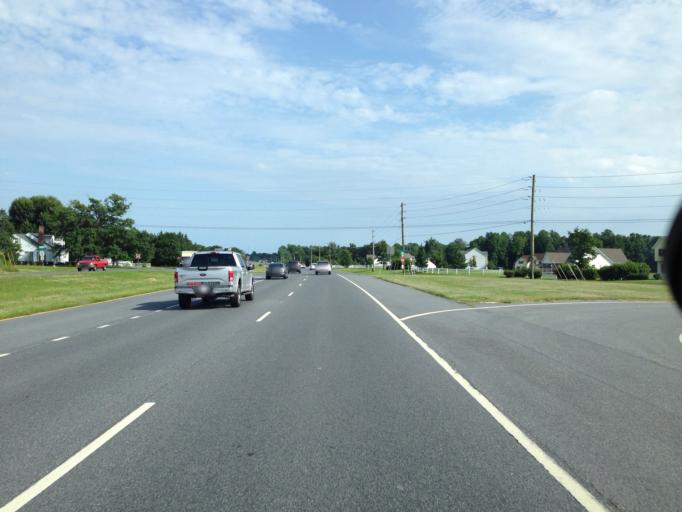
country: US
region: Delaware
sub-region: Sussex County
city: Milton
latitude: 38.8296
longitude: -75.3130
